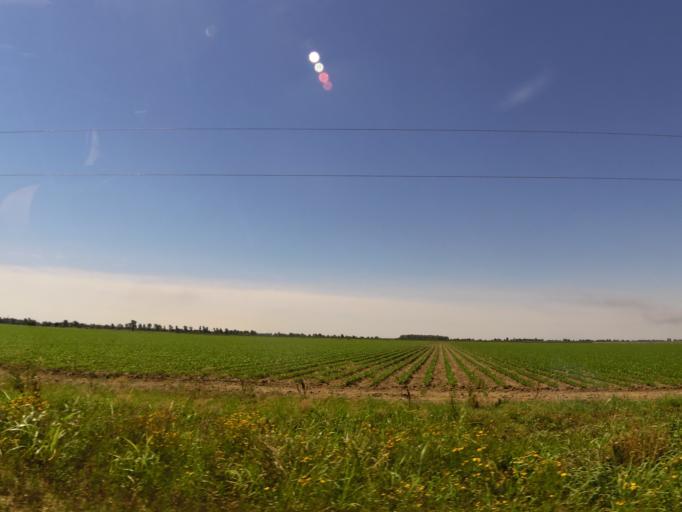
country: US
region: Missouri
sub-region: New Madrid County
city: Lilbourn
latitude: 36.5538
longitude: -89.6905
